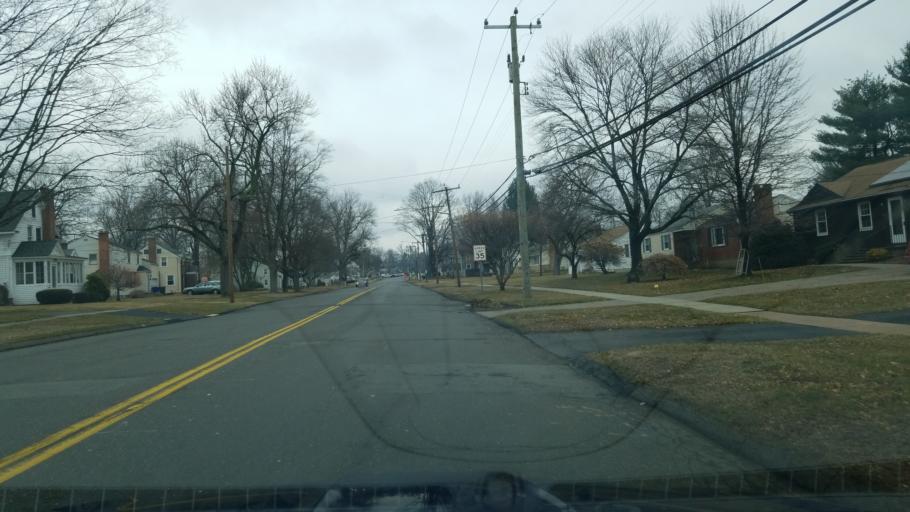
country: US
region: Connecticut
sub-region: Hartford County
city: Wethersfield
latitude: 41.6951
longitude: -72.6676
